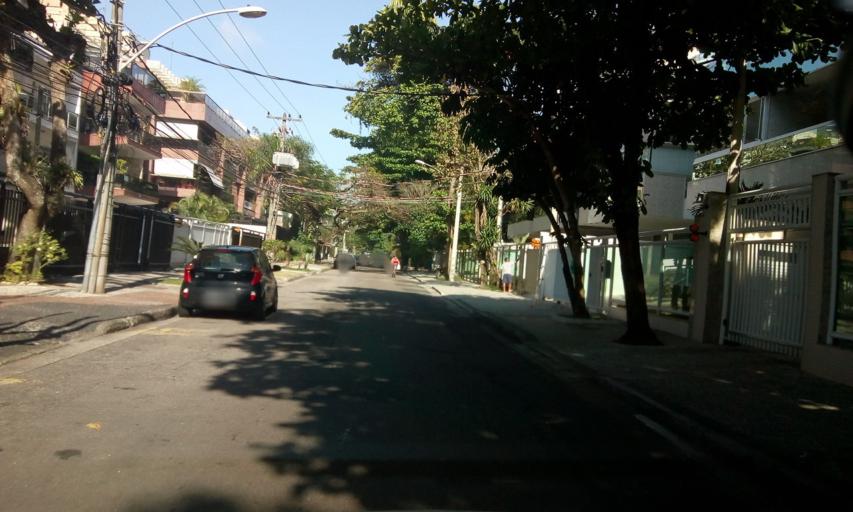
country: BR
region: Rio de Janeiro
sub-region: Rio De Janeiro
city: Rio de Janeiro
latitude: -23.0136
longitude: -43.3000
